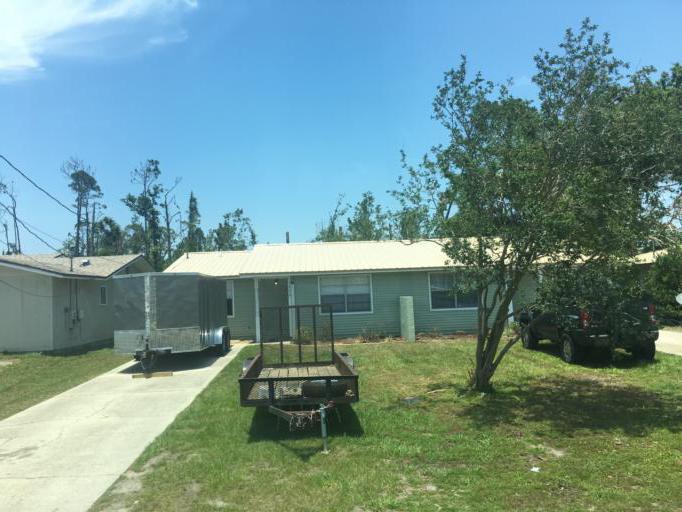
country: US
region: Florida
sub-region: Bay County
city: Lynn Haven
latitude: 30.2210
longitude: -85.6613
